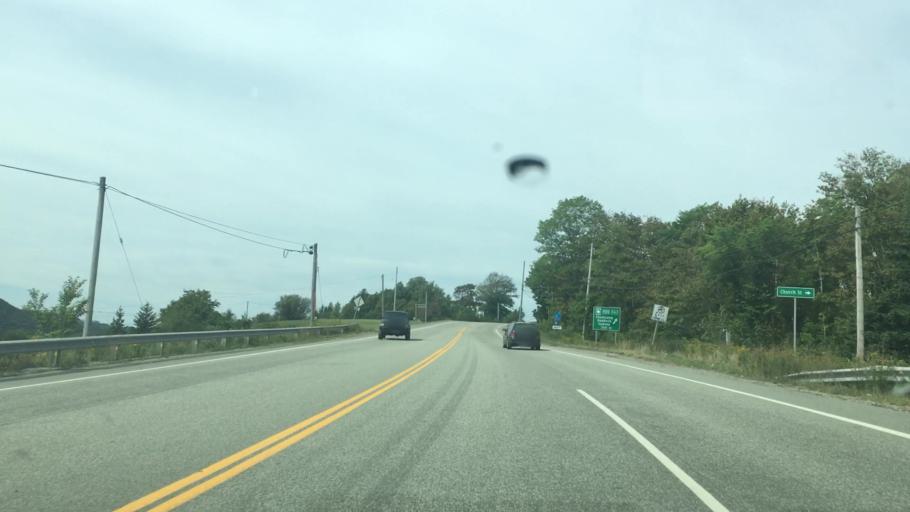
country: CA
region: Nova Scotia
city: Port Hawkesbury
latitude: 45.6446
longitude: -61.3976
